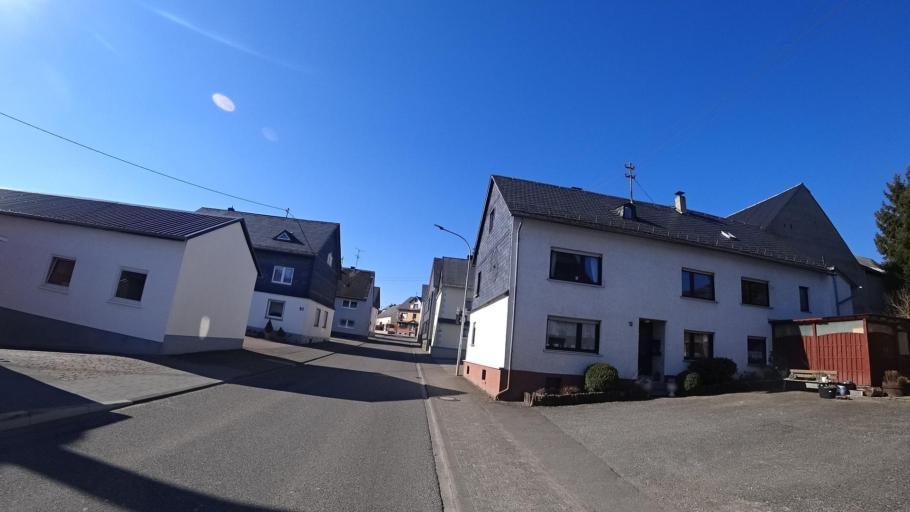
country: DE
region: Rheinland-Pfalz
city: Holzbach
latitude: 49.9552
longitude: 7.5320
